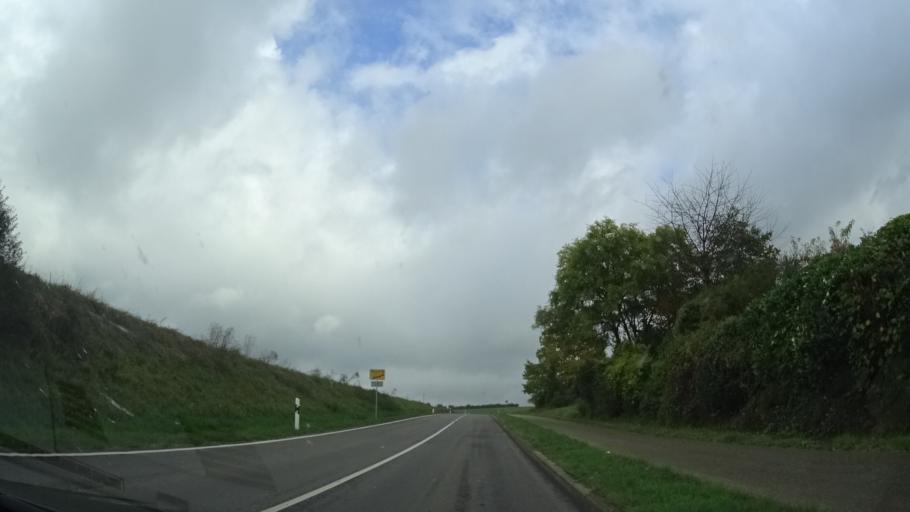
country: DE
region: Baden-Wuerttemberg
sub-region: Karlsruhe Region
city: Konigsbach-Stein
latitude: 48.9678
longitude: 8.6351
